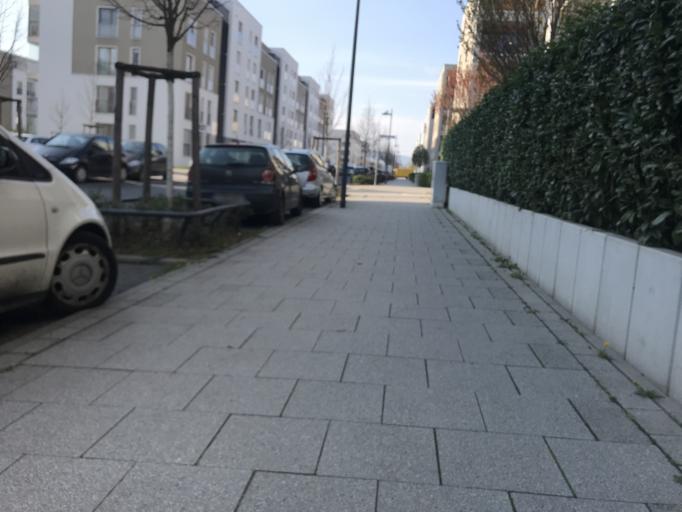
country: DE
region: Hesse
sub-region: Regierungsbezirk Darmstadt
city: Bad Homburg vor der Hoehe
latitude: 50.1759
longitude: 8.6269
